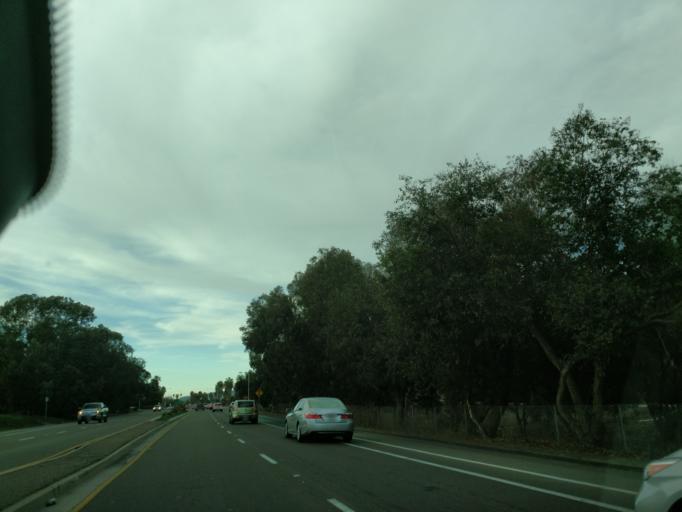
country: US
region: California
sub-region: San Diego County
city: Coronado
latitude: 32.7487
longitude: -117.2349
